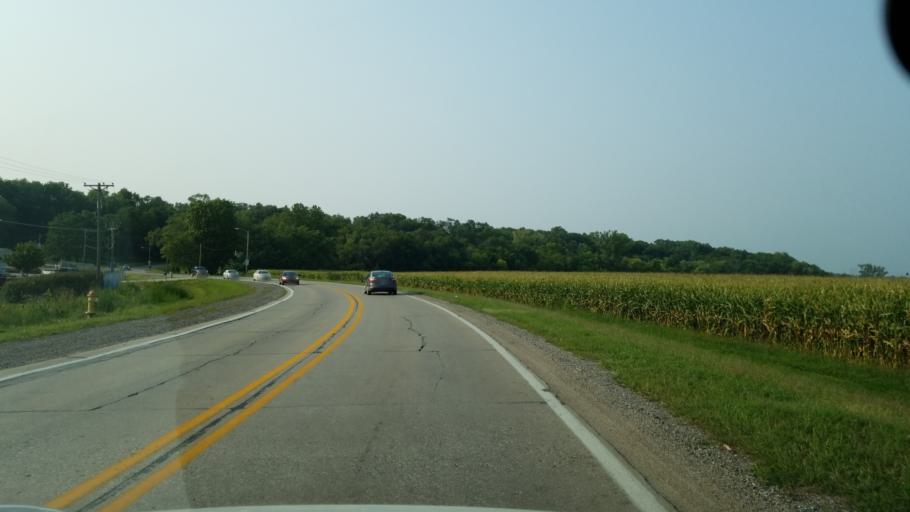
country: US
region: Nebraska
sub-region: Sarpy County
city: Bellevue
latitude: 41.1265
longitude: -95.8902
